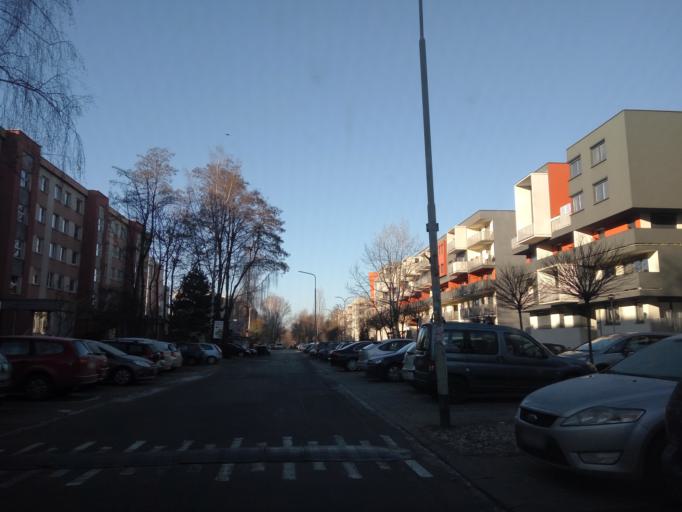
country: PL
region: Lower Silesian Voivodeship
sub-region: Powiat wroclawski
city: Wroclaw
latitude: 51.1254
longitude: 16.9600
